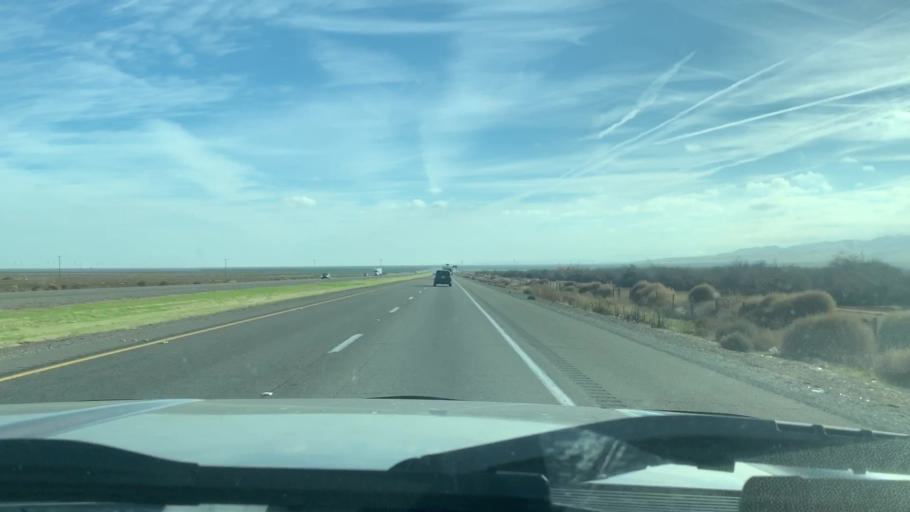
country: US
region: California
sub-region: Merced County
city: South Dos Palos
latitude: 36.8163
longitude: -120.7508
